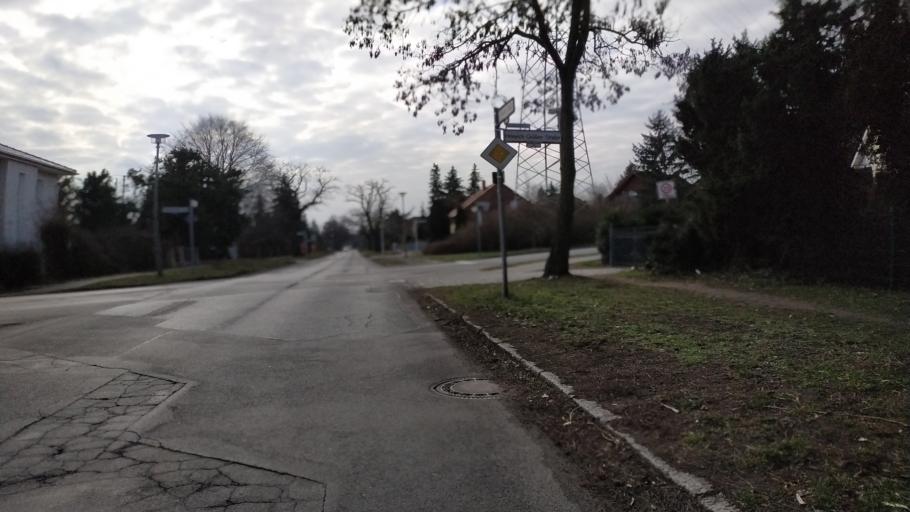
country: DE
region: Berlin
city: Hellersdorf
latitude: 52.5248
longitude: 13.6062
